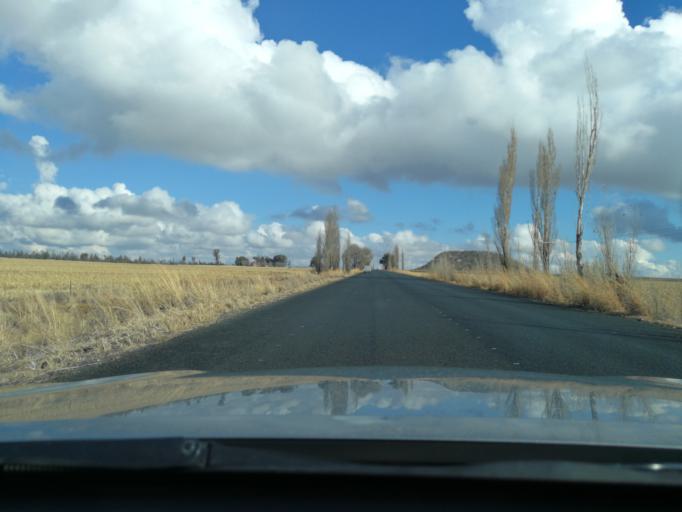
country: ZA
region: Orange Free State
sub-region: Thabo Mofutsanyana District Municipality
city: Reitz
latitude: -27.8890
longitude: 28.3975
